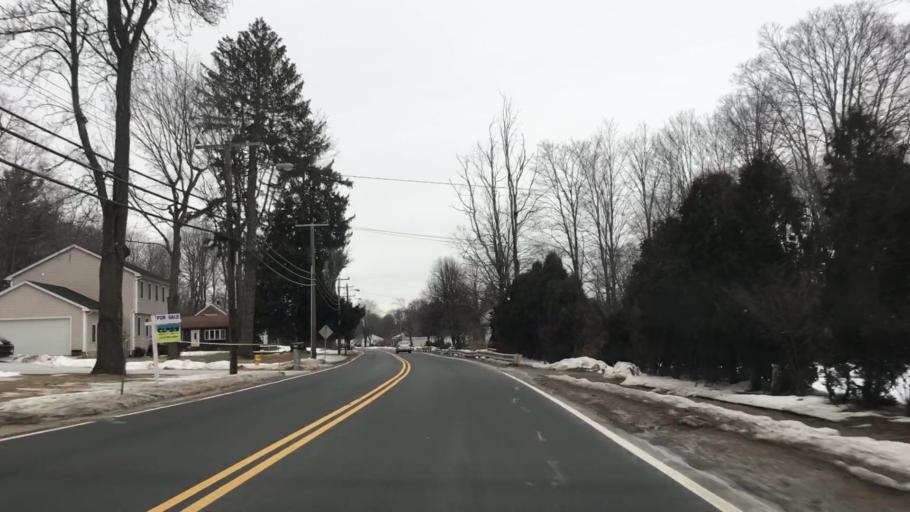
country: US
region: Massachusetts
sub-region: Hampden County
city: West Springfield
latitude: 42.0805
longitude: -72.6790
